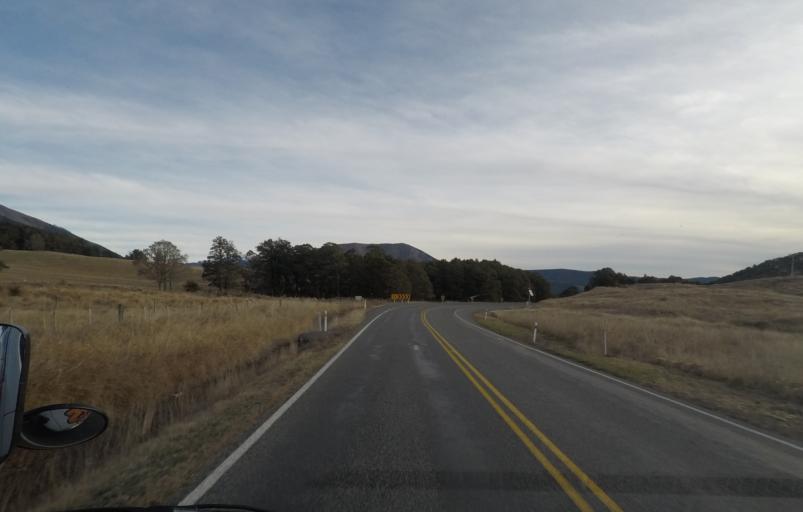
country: NZ
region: Tasman
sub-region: Tasman District
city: Wakefield
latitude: -41.7991
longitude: 172.8683
